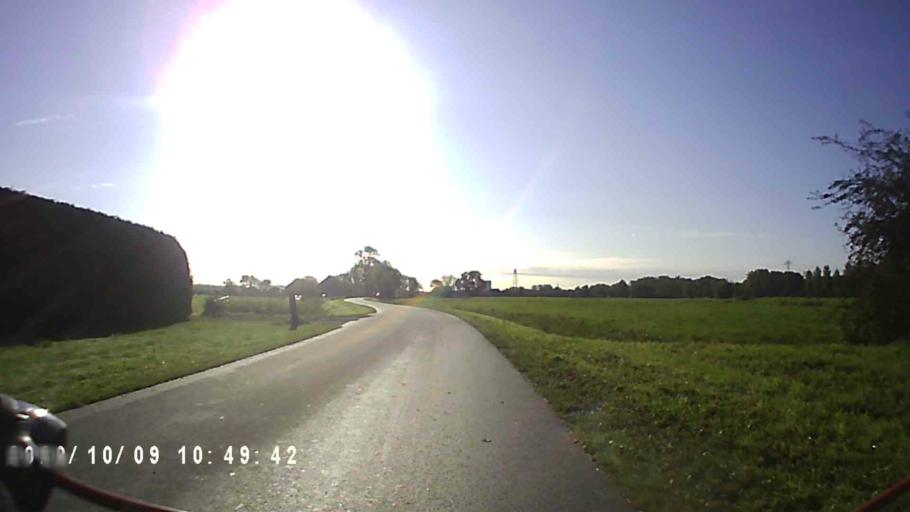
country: NL
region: Groningen
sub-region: Gemeente Groningen
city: Korrewegwijk
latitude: 53.2521
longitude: 6.5474
